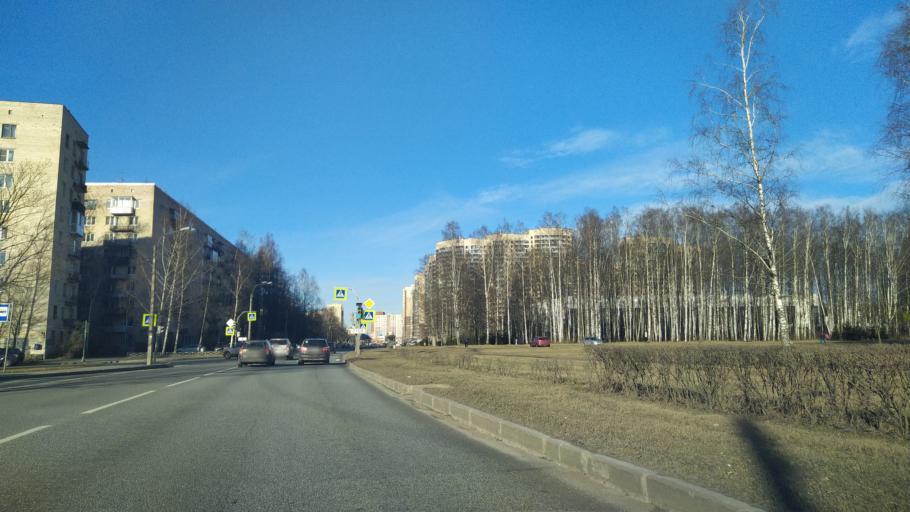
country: RU
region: Leningrad
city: Kalininskiy
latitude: 59.9996
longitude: 30.3945
